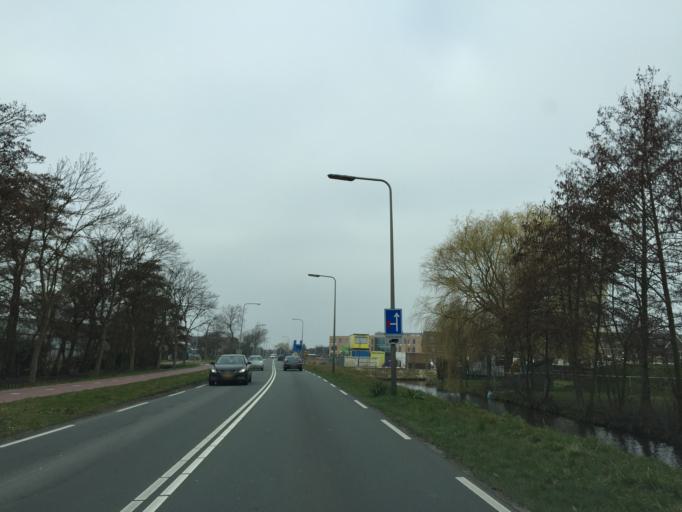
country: NL
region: South Holland
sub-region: Gemeente Westland
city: Naaldwijk
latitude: 51.9848
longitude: 4.2040
